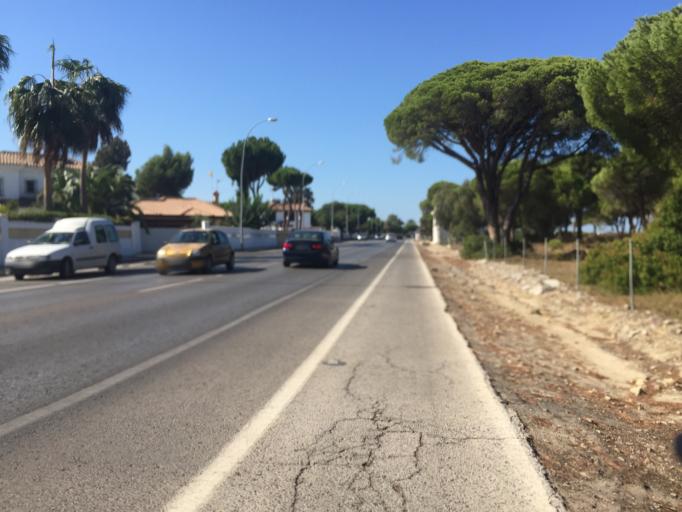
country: ES
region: Andalusia
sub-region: Provincia de Cadiz
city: Chiclana de la Frontera
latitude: 36.3901
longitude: -6.1818
